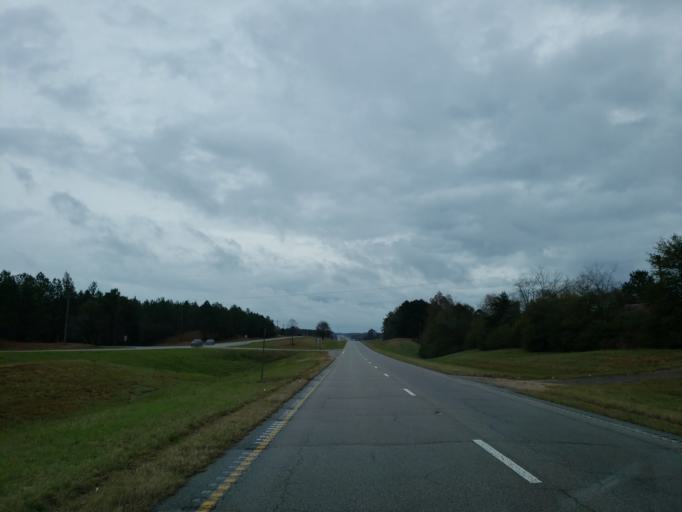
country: US
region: Mississippi
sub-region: Wayne County
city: Waynesboro
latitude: 31.6966
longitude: -88.8689
